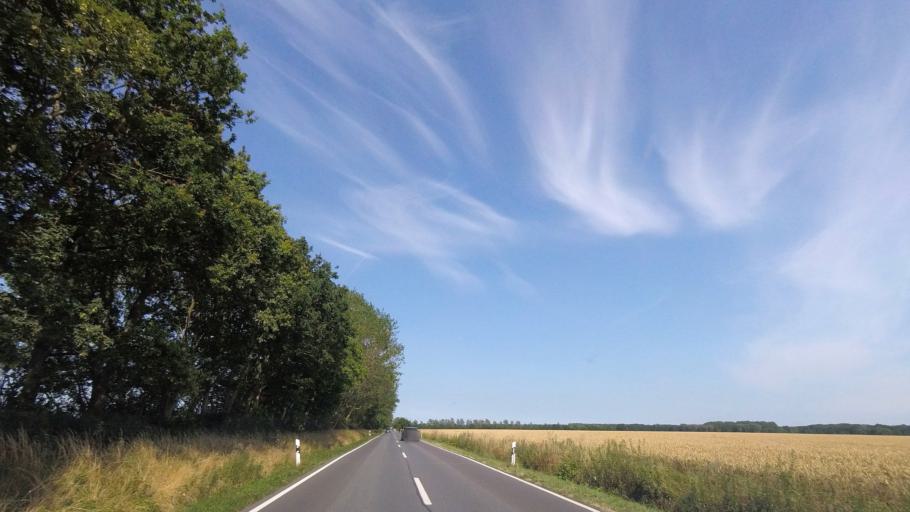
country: DE
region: Mecklenburg-Vorpommern
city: Gingst
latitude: 54.4632
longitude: 13.2791
